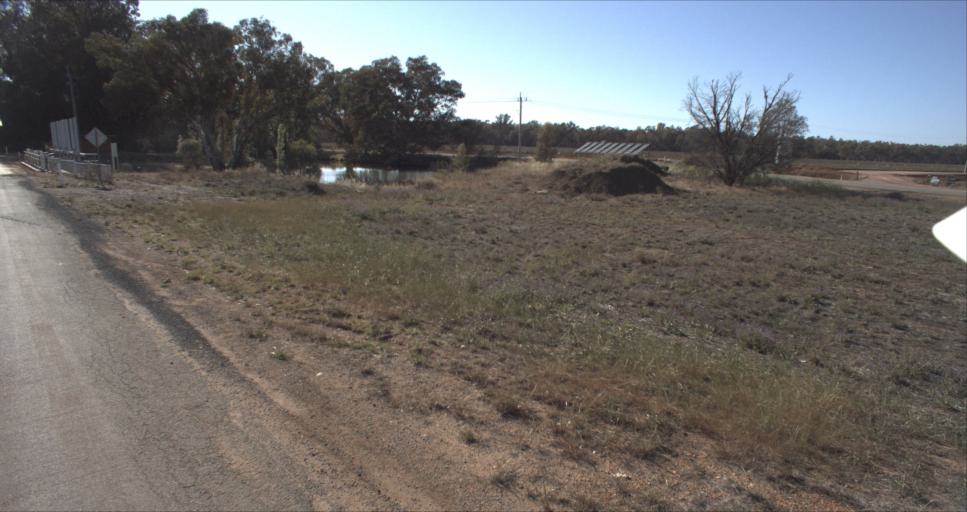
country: AU
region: New South Wales
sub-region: Leeton
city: Leeton
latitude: -34.6059
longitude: 146.2556
